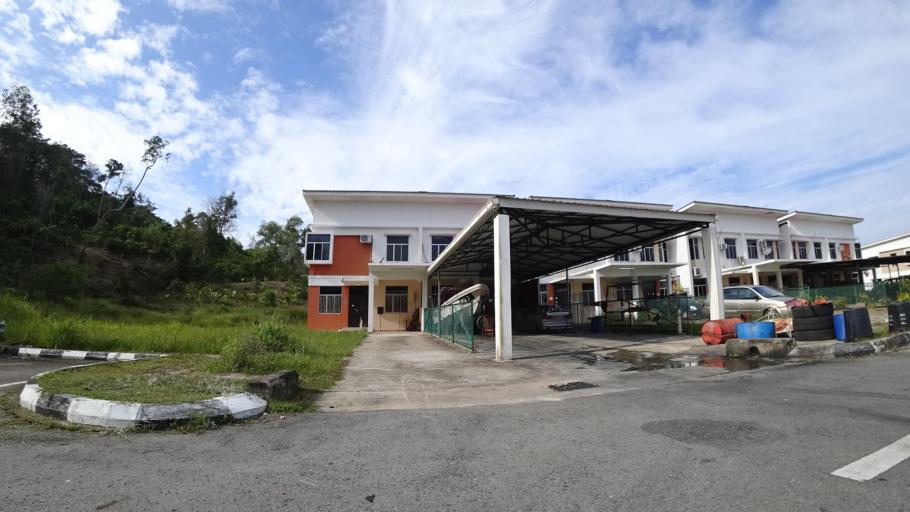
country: BN
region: Brunei and Muara
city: Bandar Seri Begawan
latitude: 4.8867
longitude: 114.7966
